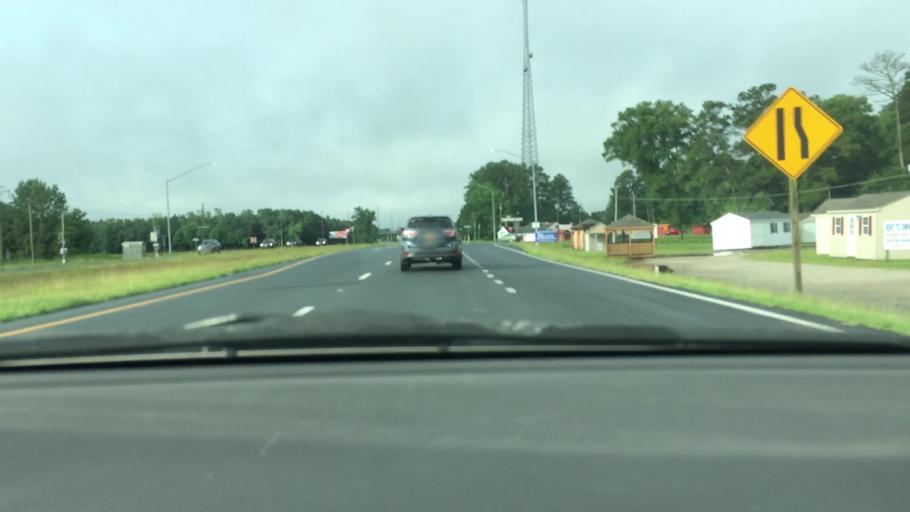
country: US
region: Maryland
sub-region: Wicomico County
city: Fruitland
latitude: 38.3082
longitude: -75.6301
